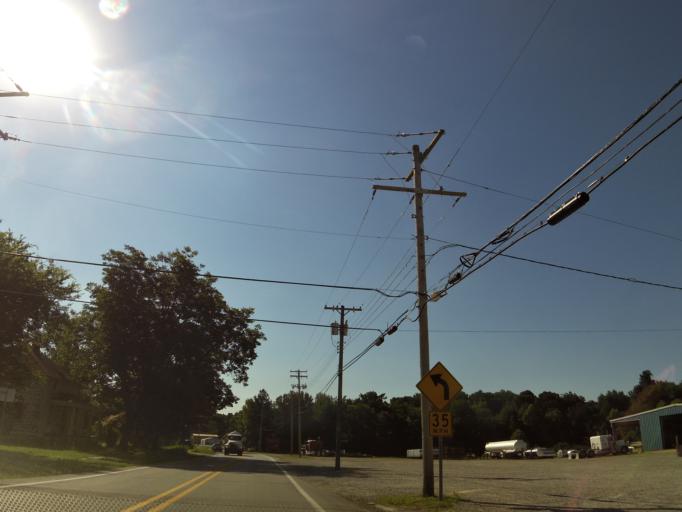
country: US
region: Arkansas
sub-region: Clay County
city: Corning
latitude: 36.4075
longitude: -90.5792
